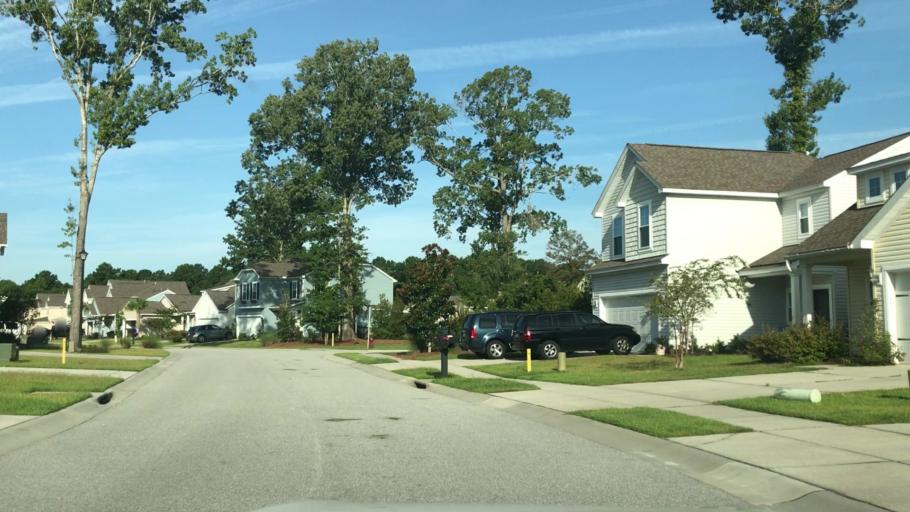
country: US
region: South Carolina
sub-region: Charleston County
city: Isle of Palms
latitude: 32.8912
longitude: -79.7513
